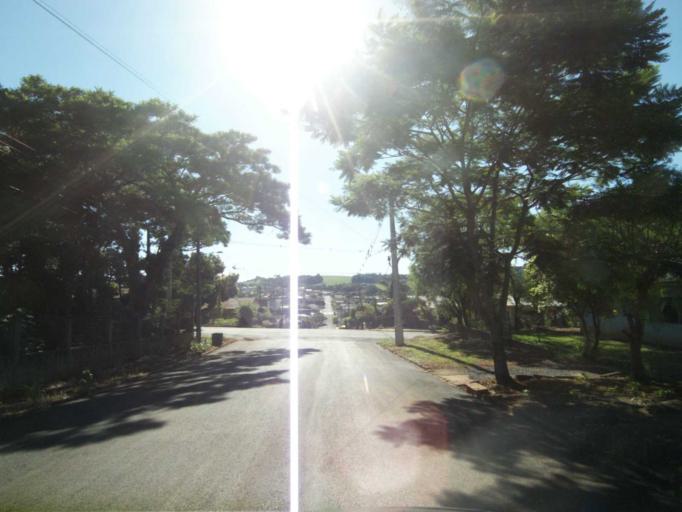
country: BR
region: Parana
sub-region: Coronel Vivida
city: Coronel Vivida
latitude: -25.9688
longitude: -52.8118
